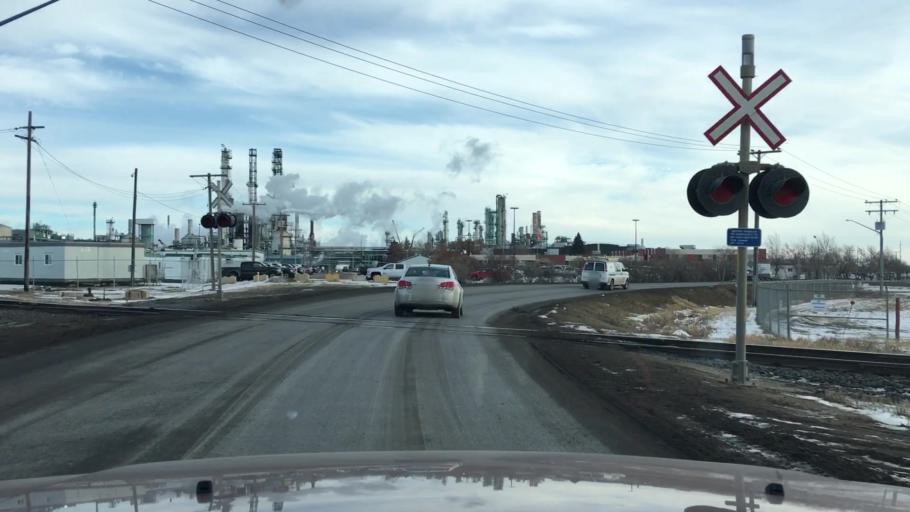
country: CA
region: Saskatchewan
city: Regina
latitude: 50.4843
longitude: -104.5828
